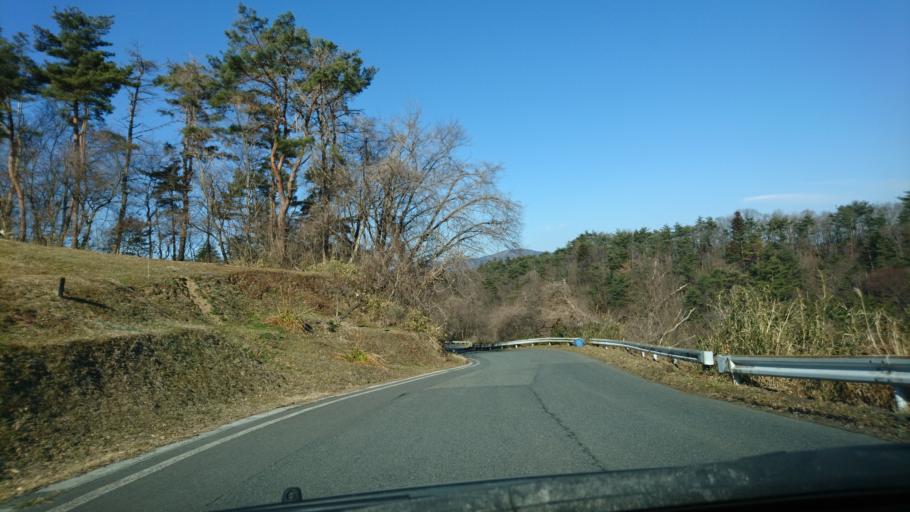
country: JP
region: Iwate
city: Ichinoseki
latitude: 38.9538
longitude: 141.1054
